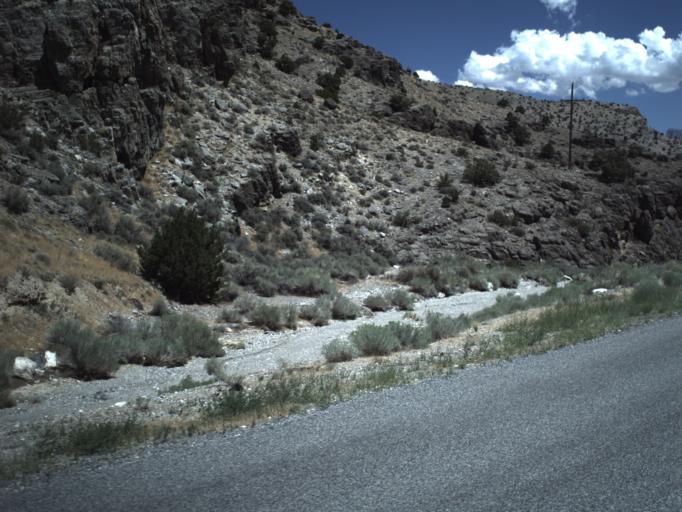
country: US
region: Utah
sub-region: Beaver County
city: Milford
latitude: 39.0823
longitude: -113.5883
